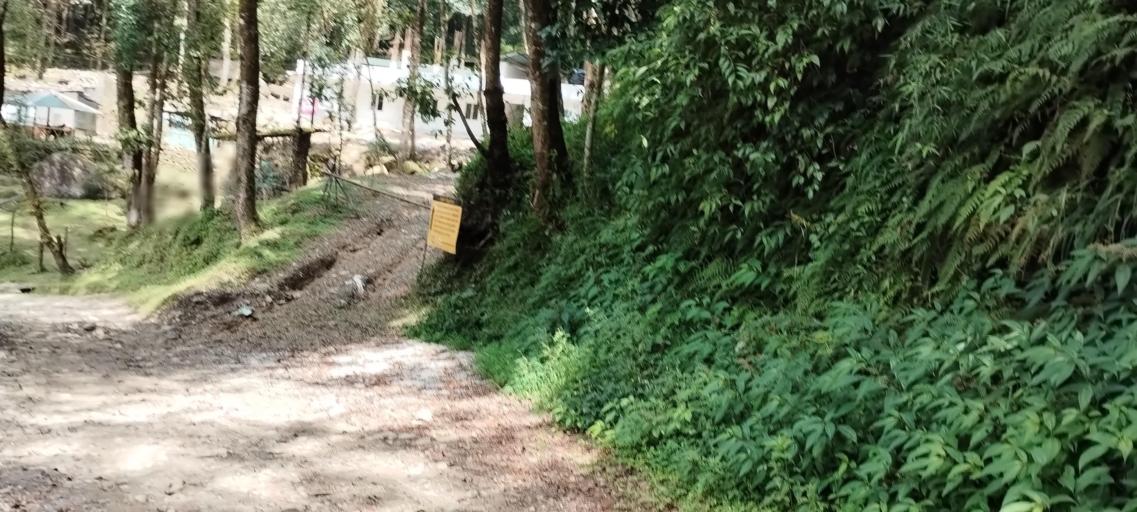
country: NP
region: Central Region
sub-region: Bagmati Zone
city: Kathmandu
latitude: 27.7910
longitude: 85.3723
